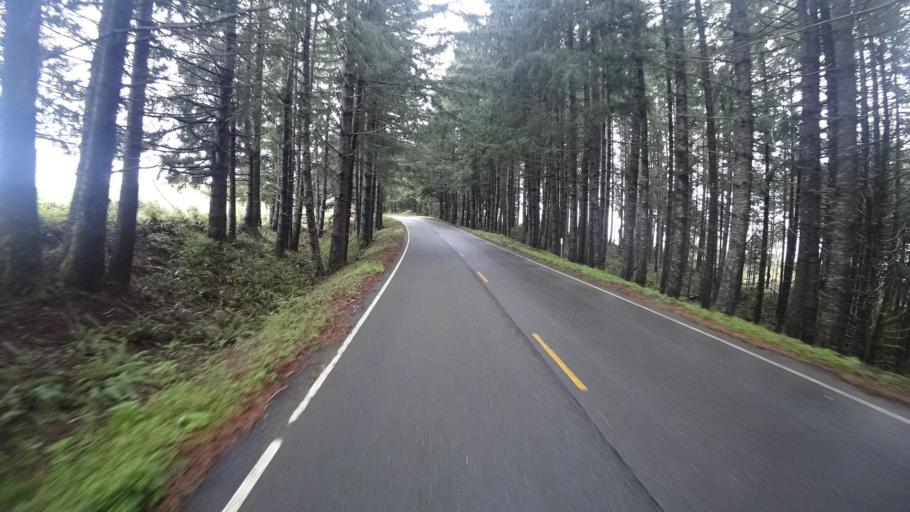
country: US
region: California
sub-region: Humboldt County
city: Westhaven-Moonstone
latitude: 41.1895
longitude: -123.9316
